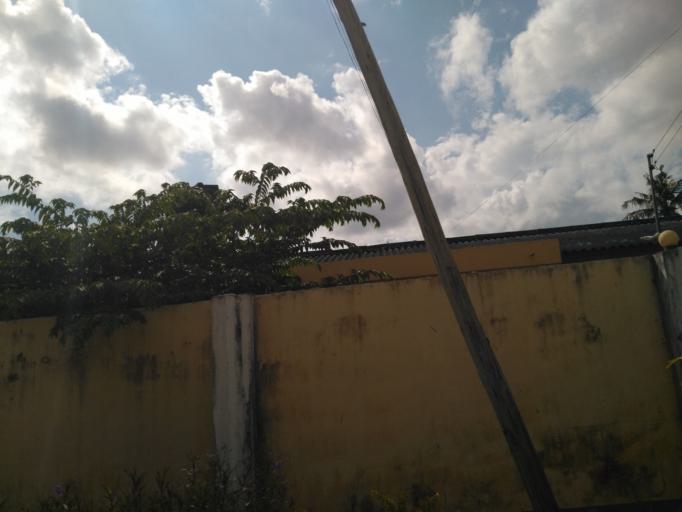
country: TZ
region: Dar es Salaam
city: Magomeni
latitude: -6.7632
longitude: 39.2447
